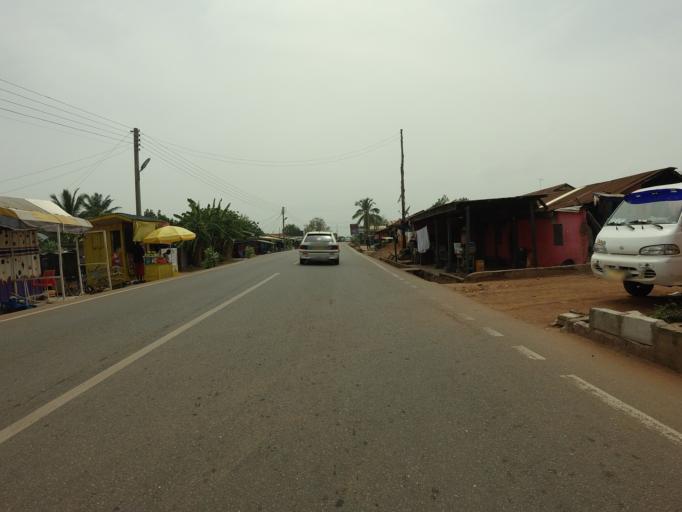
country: GH
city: Akropong
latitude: 6.0881
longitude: -0.0194
